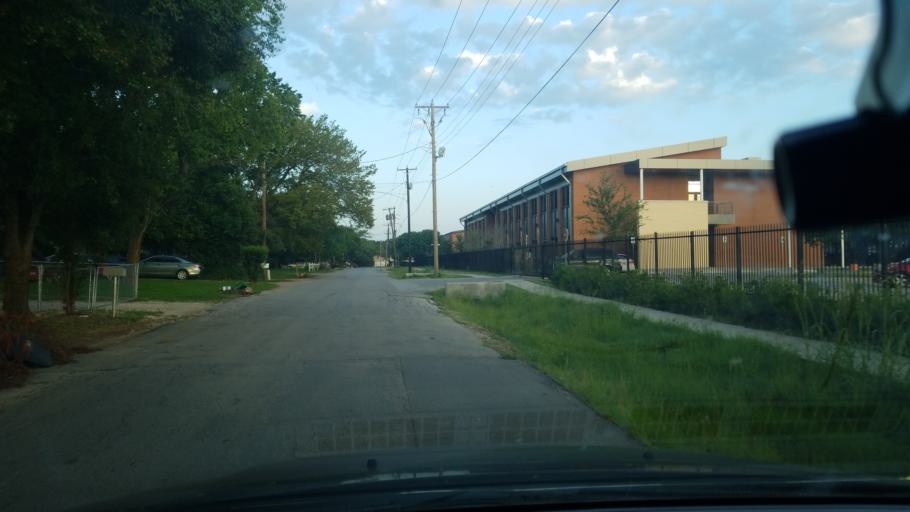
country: US
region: Texas
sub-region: Dallas County
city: Balch Springs
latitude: 32.7299
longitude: -96.6542
